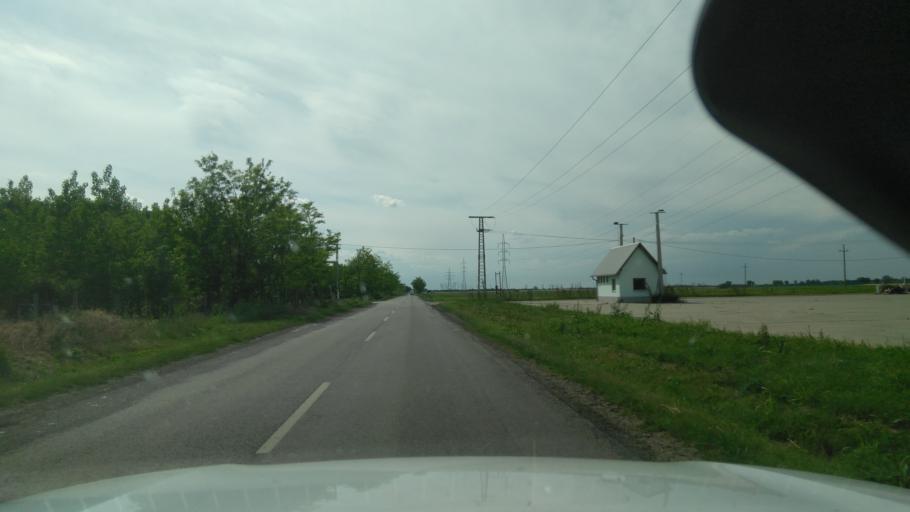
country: HU
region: Bekes
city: Medgyesegyhaza
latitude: 46.5060
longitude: 21.0087
